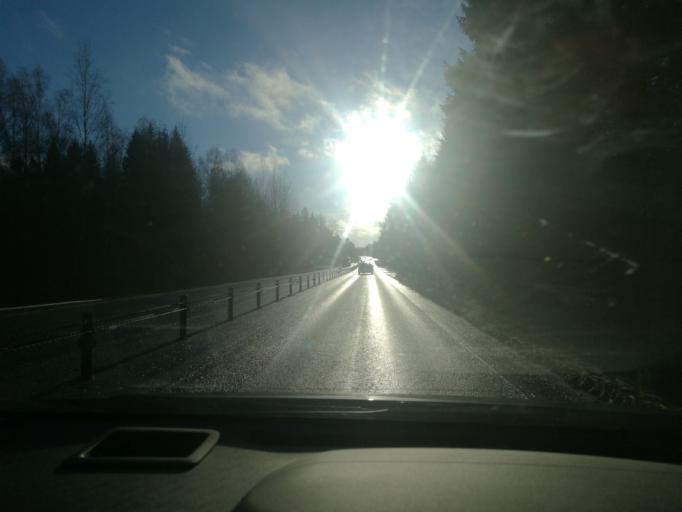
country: SE
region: OEstergoetland
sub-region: Norrkopings Kommun
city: Jursla
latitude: 58.7209
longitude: 16.1688
